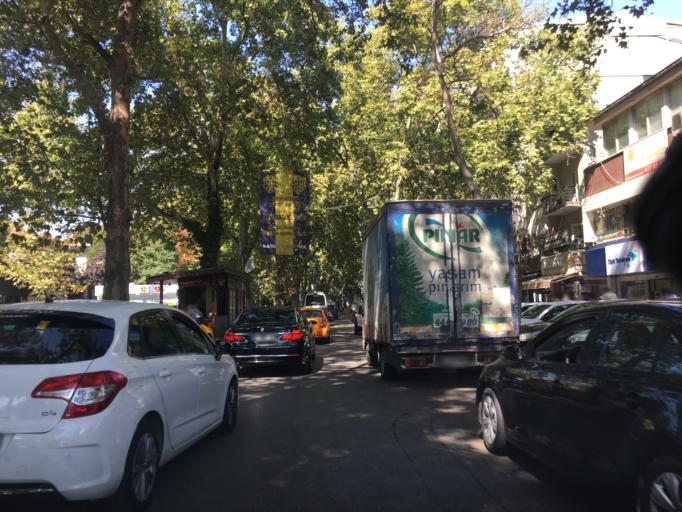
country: TR
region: Ankara
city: Ankara
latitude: 39.9193
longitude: 32.8522
